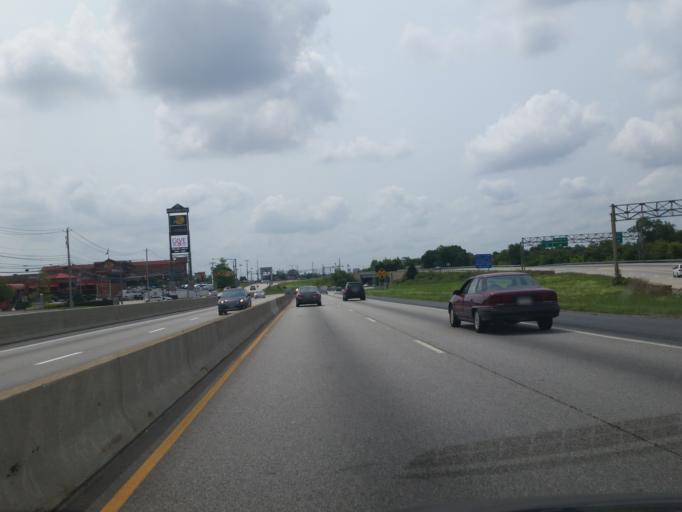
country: US
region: Pennsylvania
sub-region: Dauphin County
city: Paxtang
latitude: 40.2537
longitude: -76.8220
